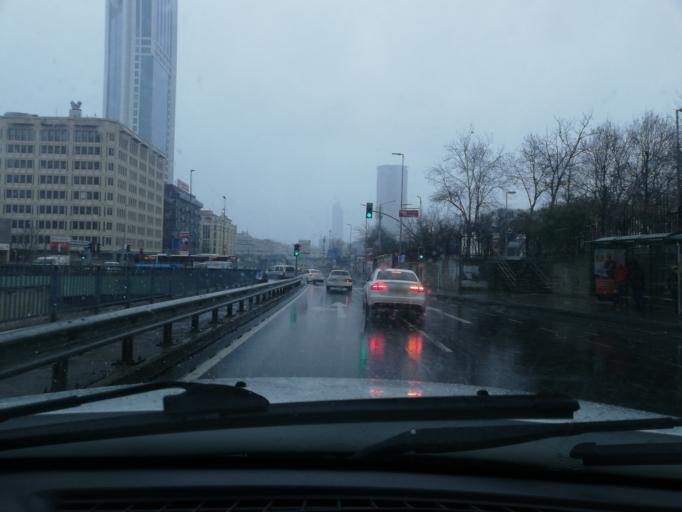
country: TR
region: Istanbul
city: Sisli
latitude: 41.0688
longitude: 28.9828
